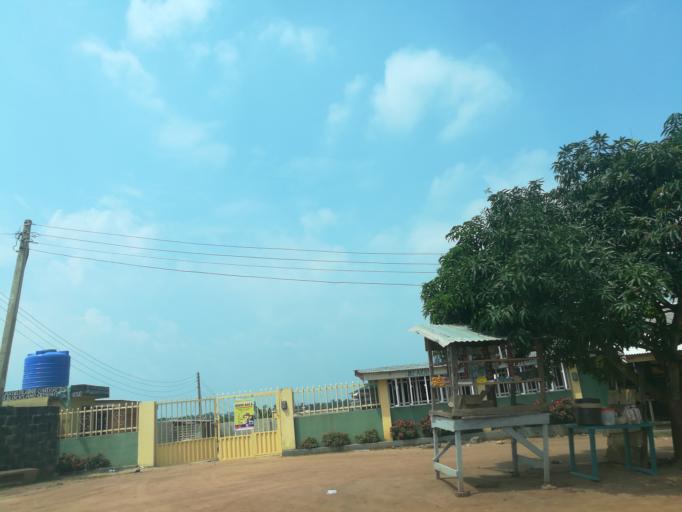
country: NG
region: Lagos
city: Ikorodu
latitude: 6.5959
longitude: 3.6332
